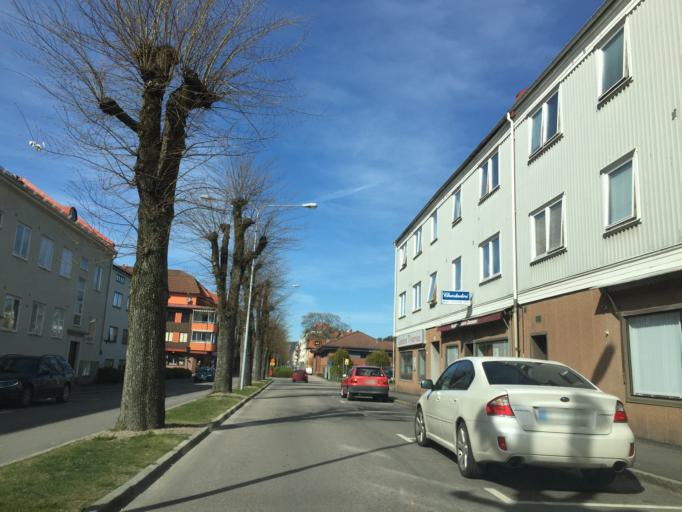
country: SE
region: Vaestra Goetaland
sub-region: Uddevalla Kommun
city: Uddevalla
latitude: 58.3438
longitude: 11.9326
